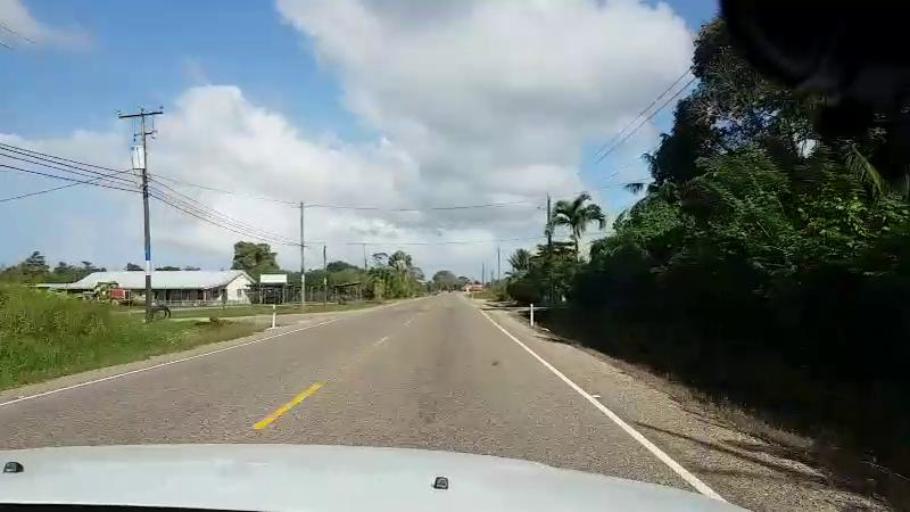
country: BZ
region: Stann Creek
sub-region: Dangriga
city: Dangriga
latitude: 16.9971
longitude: -88.3528
